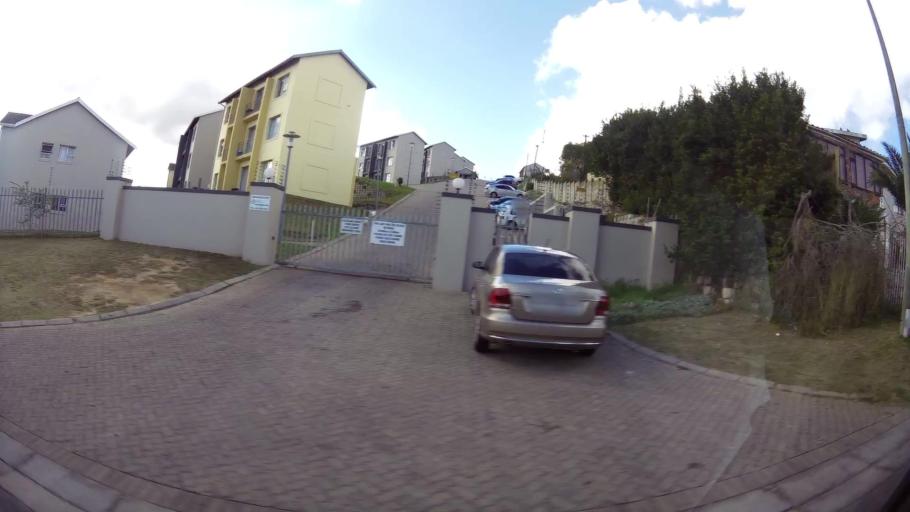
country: ZA
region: Western Cape
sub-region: Eden District Municipality
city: Knysna
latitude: -34.0481
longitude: 23.0853
